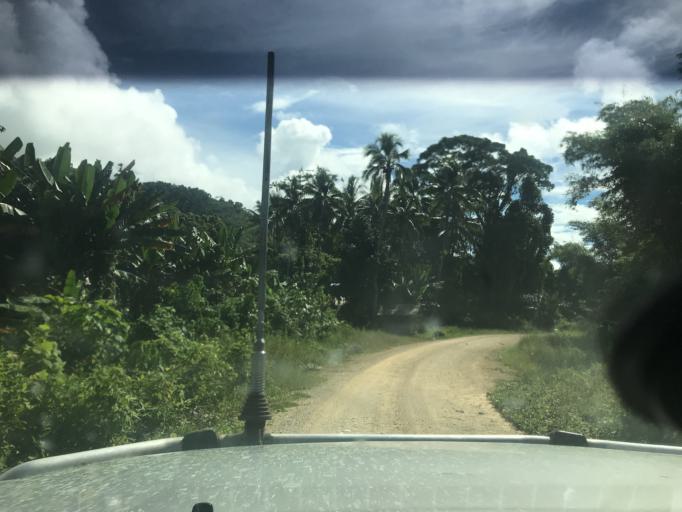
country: SB
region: Malaita
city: Auki
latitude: -8.3731
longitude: 160.6733
